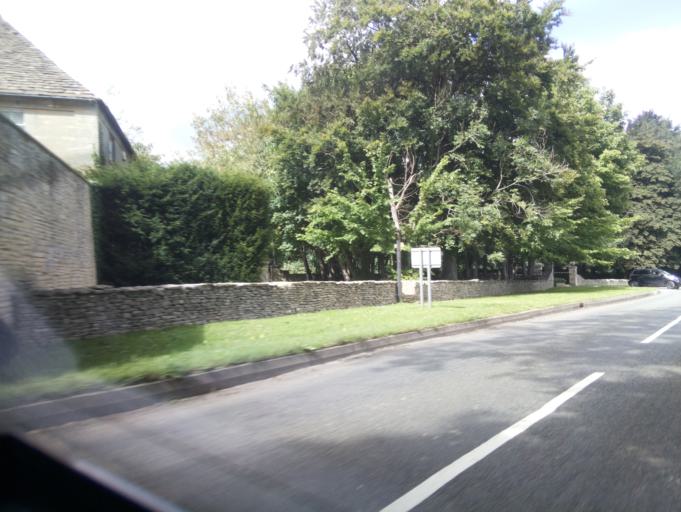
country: GB
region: England
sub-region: Wiltshire
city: Colerne
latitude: 51.4547
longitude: -2.2562
